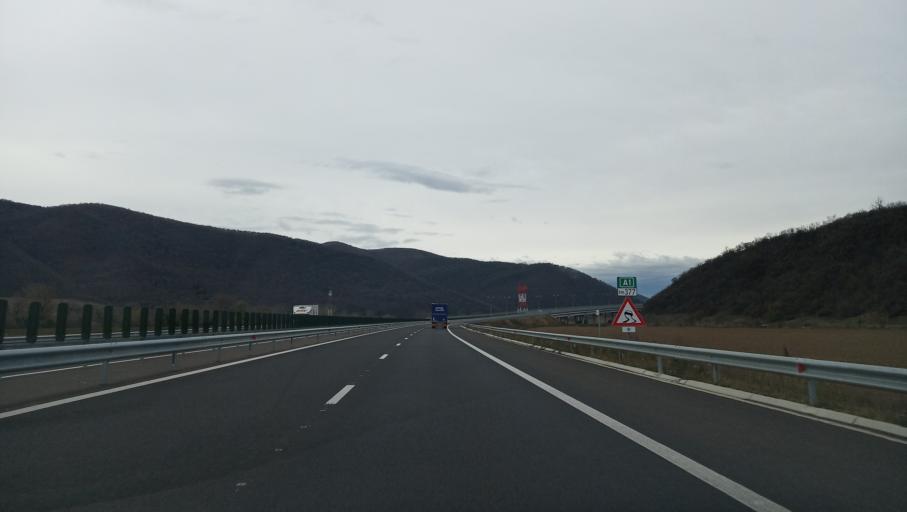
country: RO
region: Hunedoara
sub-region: Comuna Branisca
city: Branisca
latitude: 45.9115
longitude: 22.7968
